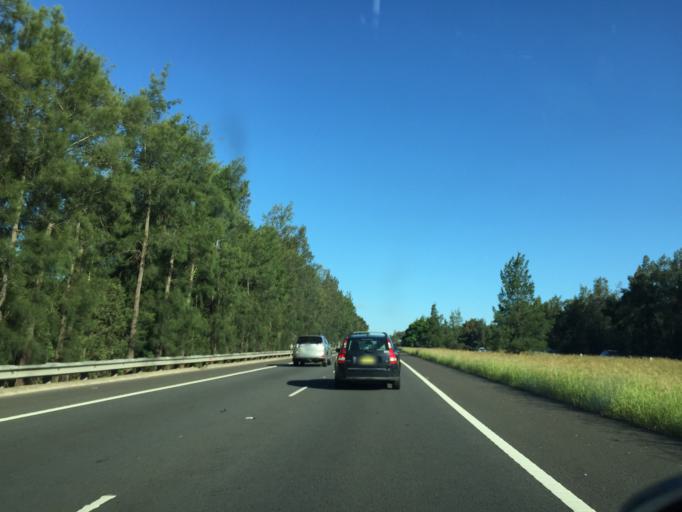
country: AU
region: New South Wales
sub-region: Penrith Municipality
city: Glenmore Park
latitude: -33.7715
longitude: 150.6688
